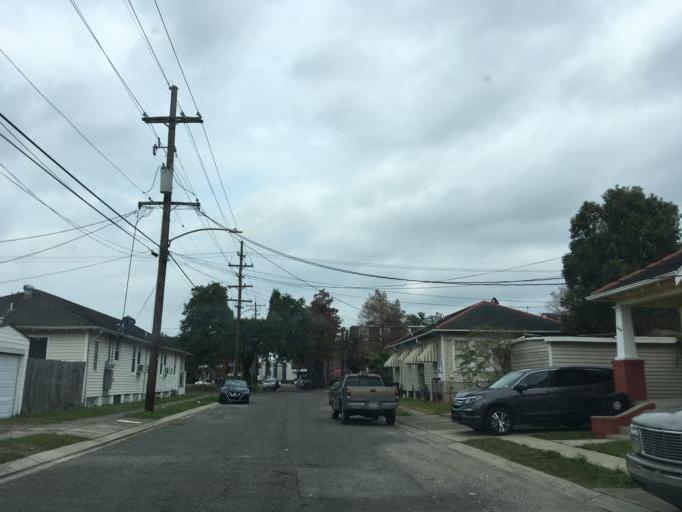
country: US
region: Louisiana
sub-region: Orleans Parish
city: New Orleans
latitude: 29.9952
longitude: -90.0614
